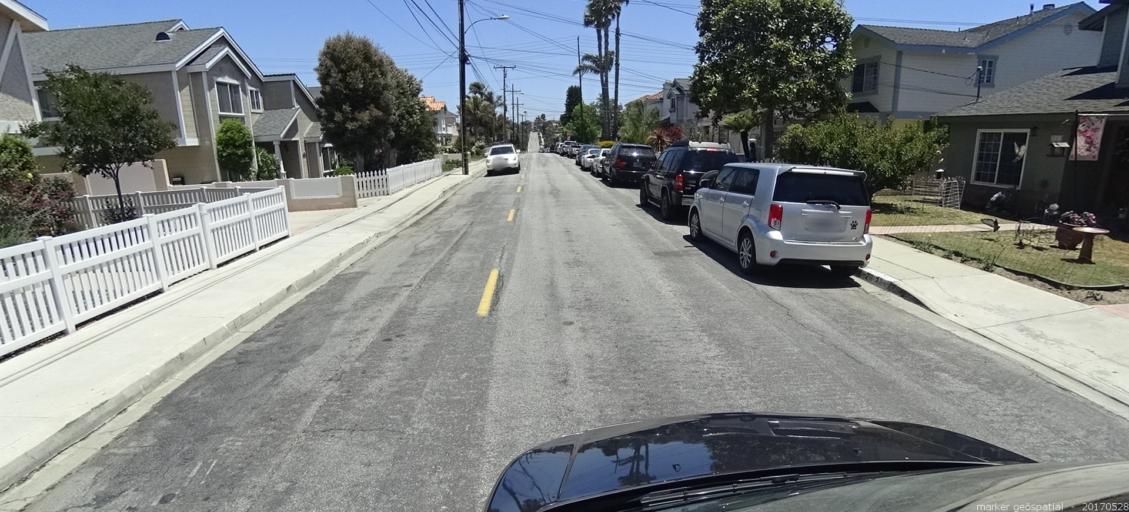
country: US
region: California
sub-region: Los Angeles County
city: Redondo Beach
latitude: 33.8634
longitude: -118.3760
